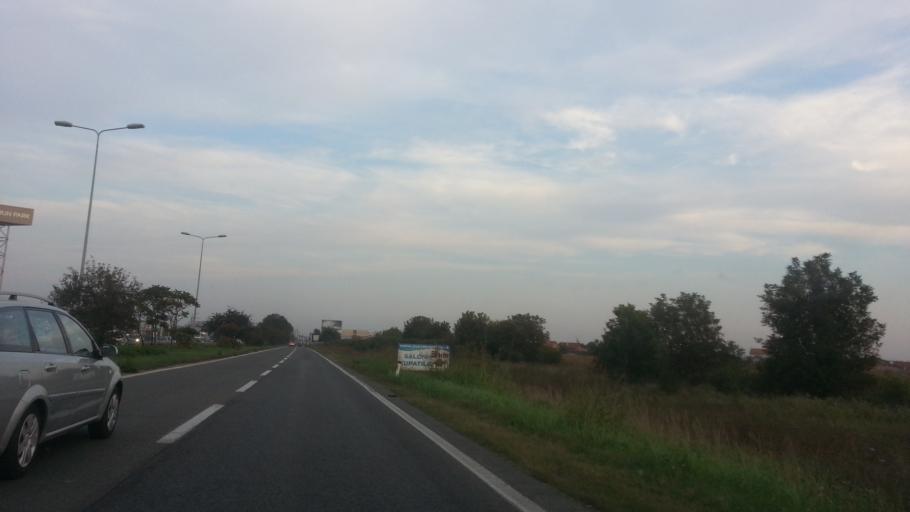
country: RS
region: Central Serbia
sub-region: Belgrade
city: Zemun
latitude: 44.8668
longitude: 20.3428
